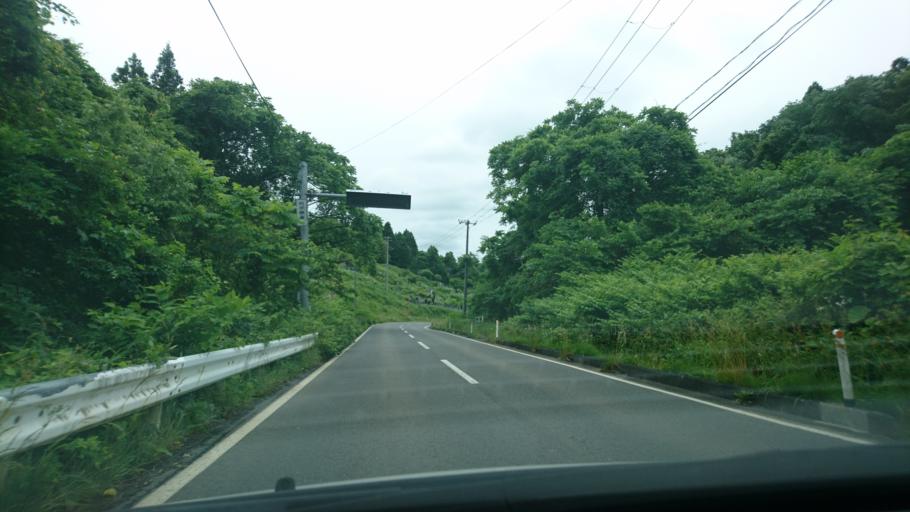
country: JP
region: Iwate
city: Ichinoseki
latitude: 38.9540
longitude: 141.0536
